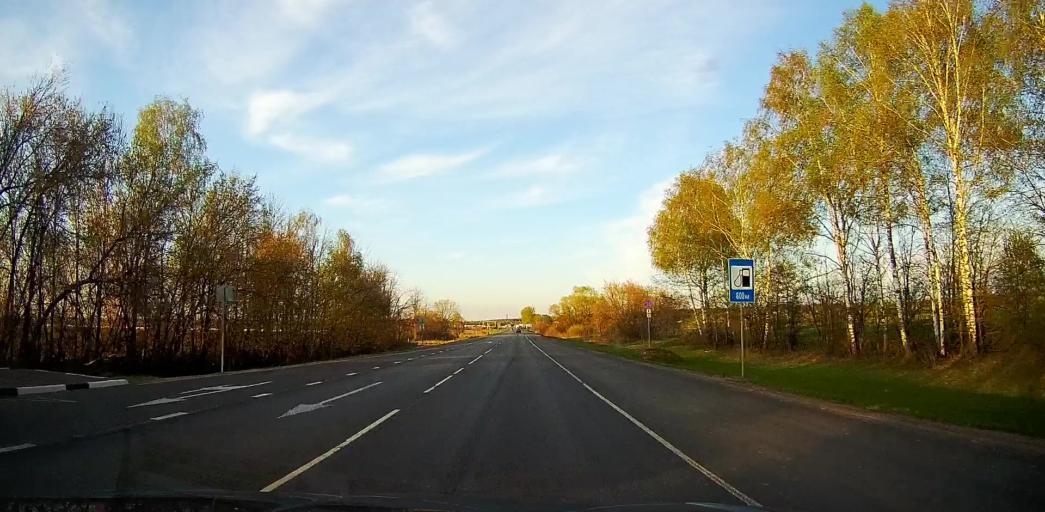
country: RU
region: Moskovskaya
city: Troitskoye
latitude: 55.2727
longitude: 38.4833
